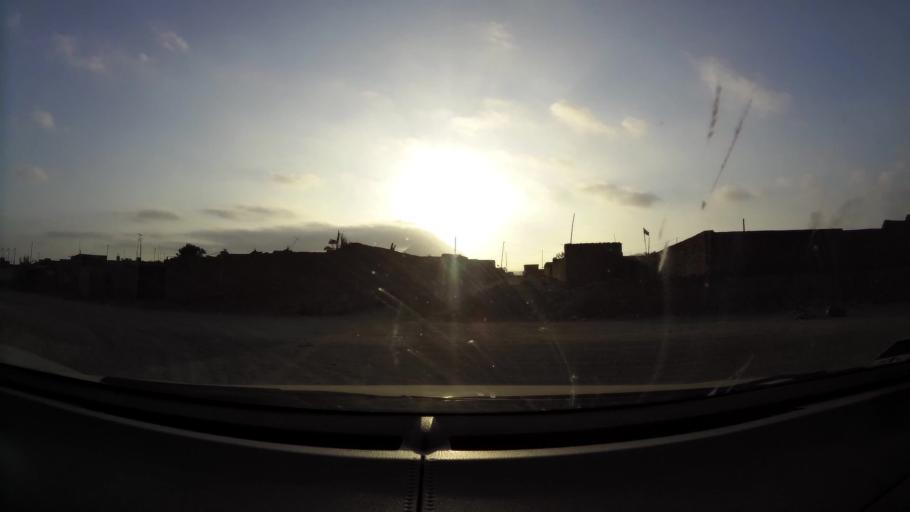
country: PE
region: La Libertad
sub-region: Provincia de Trujillo
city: El Porvenir
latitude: -8.0634
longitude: -78.9943
